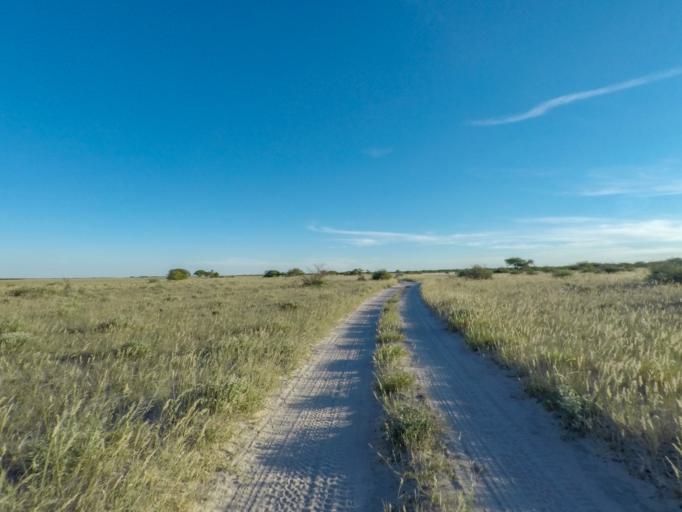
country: BW
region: Central
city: Rakops
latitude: -21.4043
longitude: 23.7961
